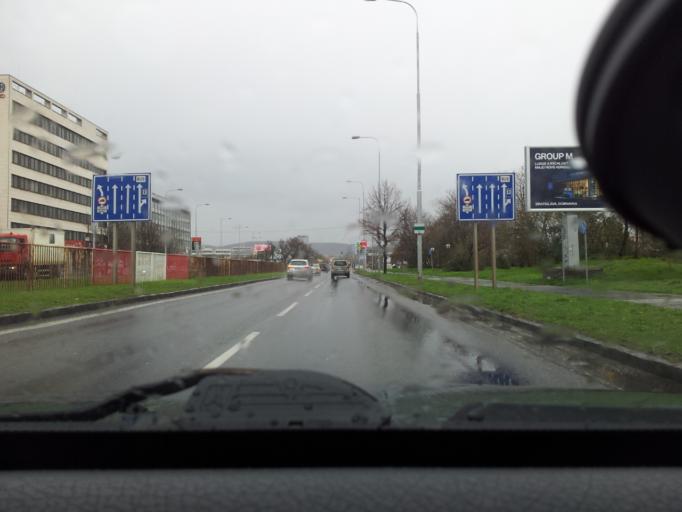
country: SK
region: Bratislavsky
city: Bratislava
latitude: 48.1520
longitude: 17.1480
